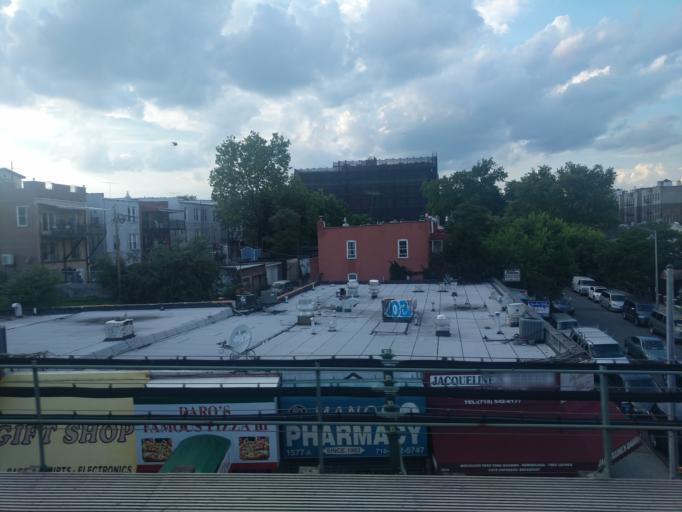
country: US
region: New York
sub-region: Bronx
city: The Bronx
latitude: 40.8290
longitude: -73.8766
